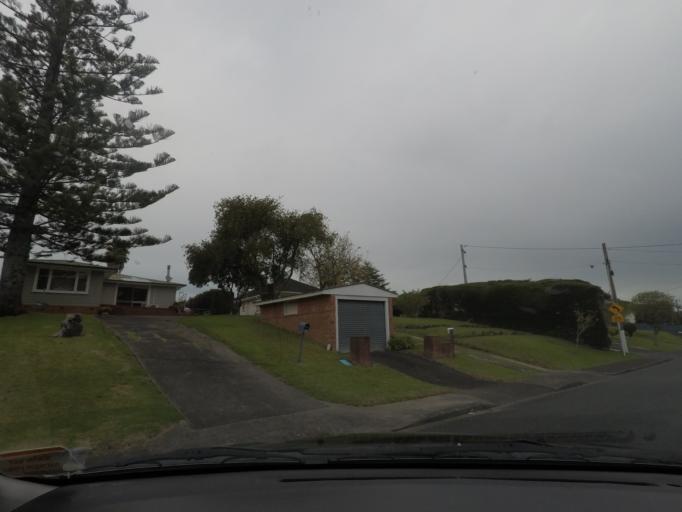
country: NZ
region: Auckland
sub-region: Auckland
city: Rosebank
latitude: -36.8619
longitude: 174.6422
